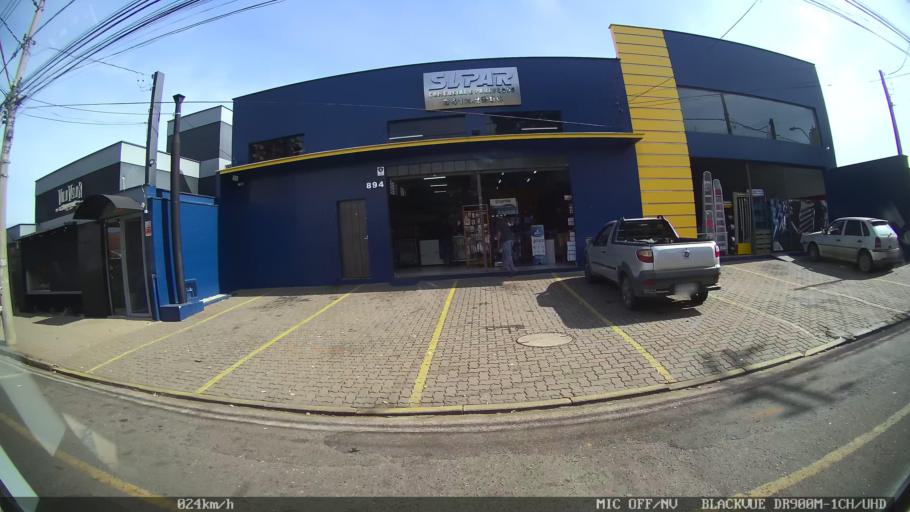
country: BR
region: Sao Paulo
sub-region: Piracicaba
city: Piracicaba
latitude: -22.7146
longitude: -47.6575
